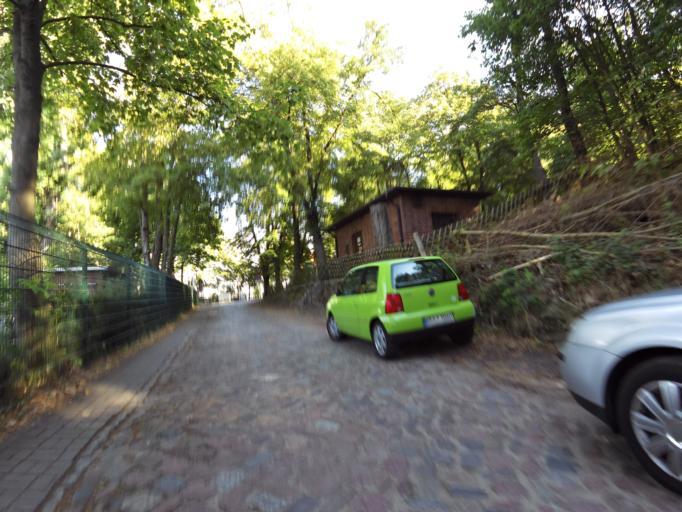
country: DE
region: Berlin
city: Nikolassee
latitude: 52.4445
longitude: 13.1768
